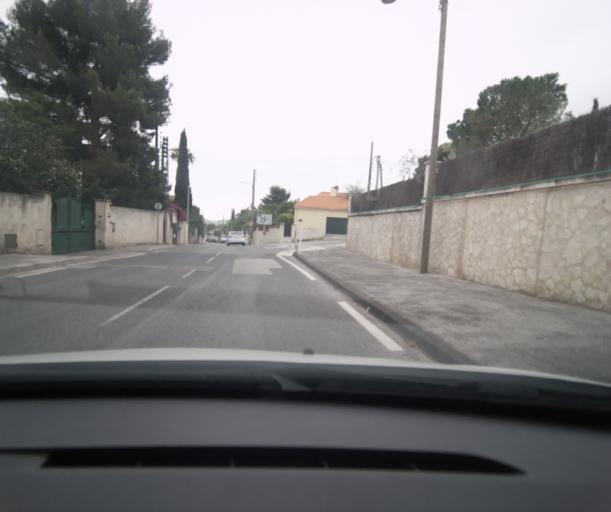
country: FR
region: Provence-Alpes-Cote d'Azur
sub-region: Departement du Var
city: La Valette-du-Var
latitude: 43.1369
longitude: 5.9776
